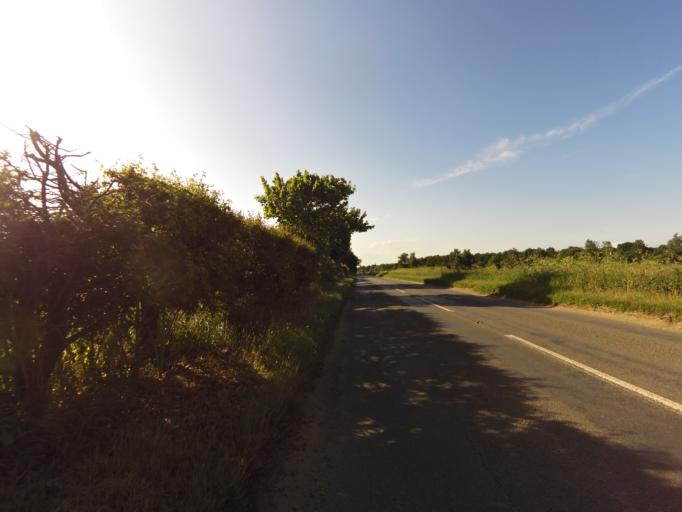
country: GB
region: England
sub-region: Suffolk
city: Woodbridge
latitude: 52.0882
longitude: 1.3557
